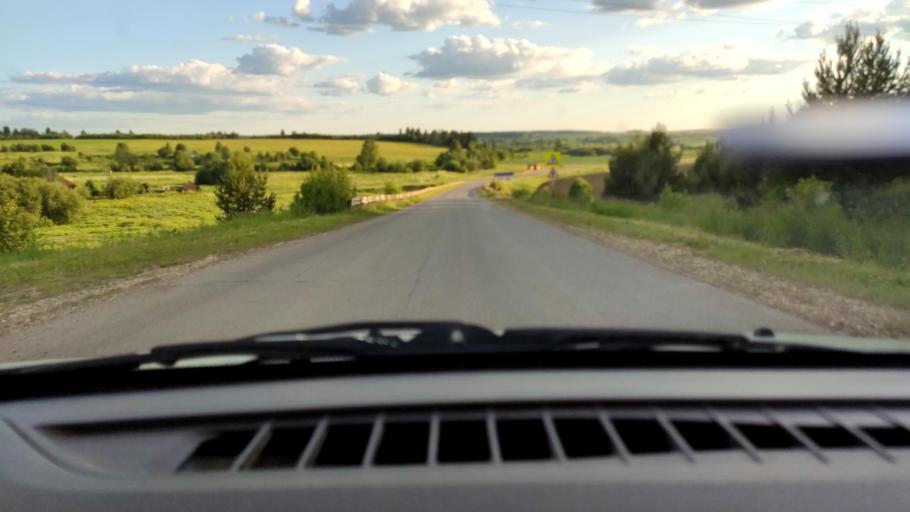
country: RU
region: Perm
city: Uinskoye
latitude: 57.0784
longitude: 56.6104
